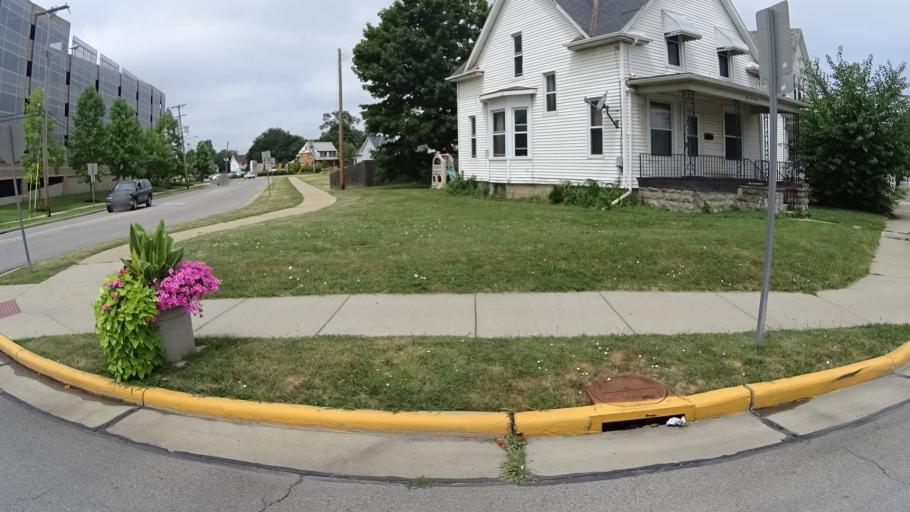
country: US
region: Ohio
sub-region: Erie County
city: Sandusky
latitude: 41.4471
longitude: -82.7084
